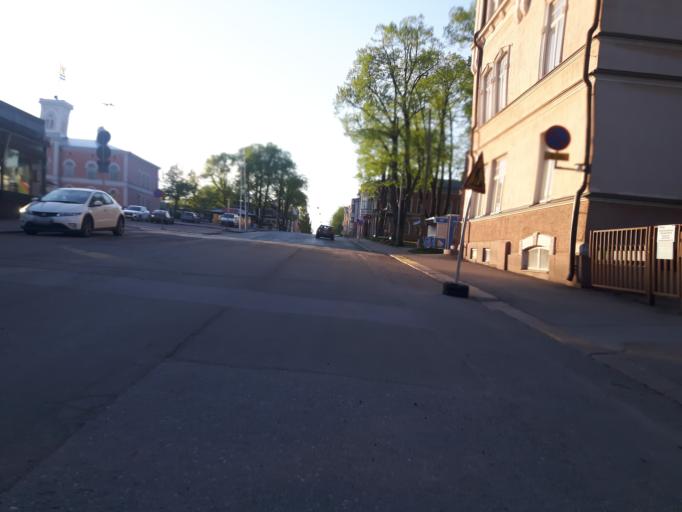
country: FI
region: Uusimaa
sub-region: Loviisa
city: Lovisa
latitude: 60.4567
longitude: 26.2268
